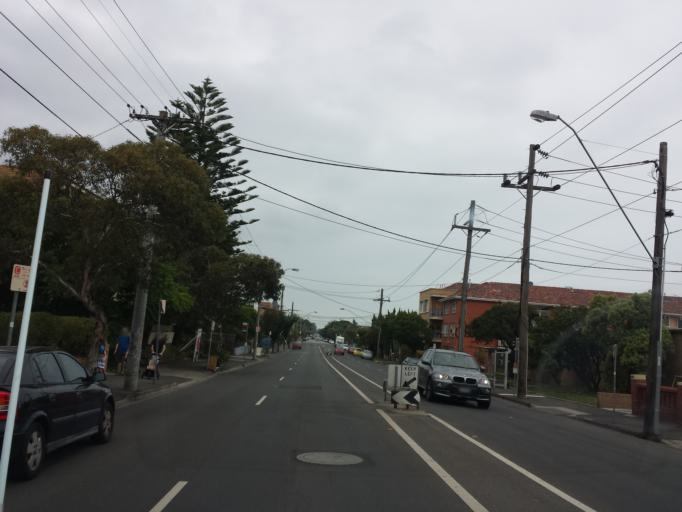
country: AU
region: Victoria
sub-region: Port Phillip
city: St Kilda East
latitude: -37.8643
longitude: 145.0004
